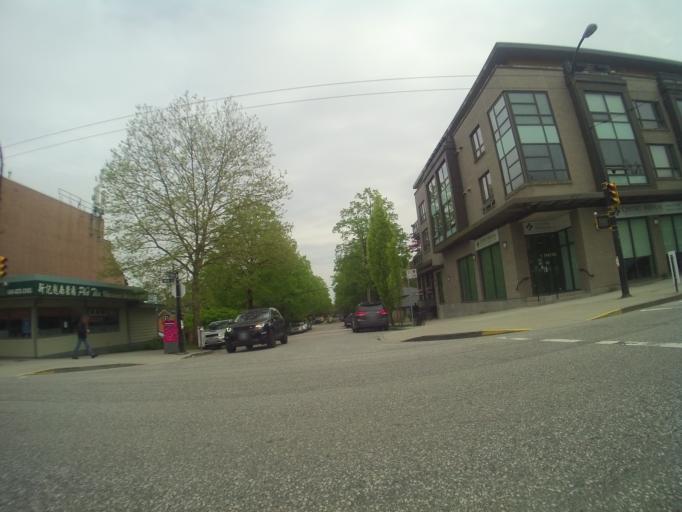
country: CA
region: British Columbia
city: Vancouver
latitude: 49.2433
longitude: -123.1015
